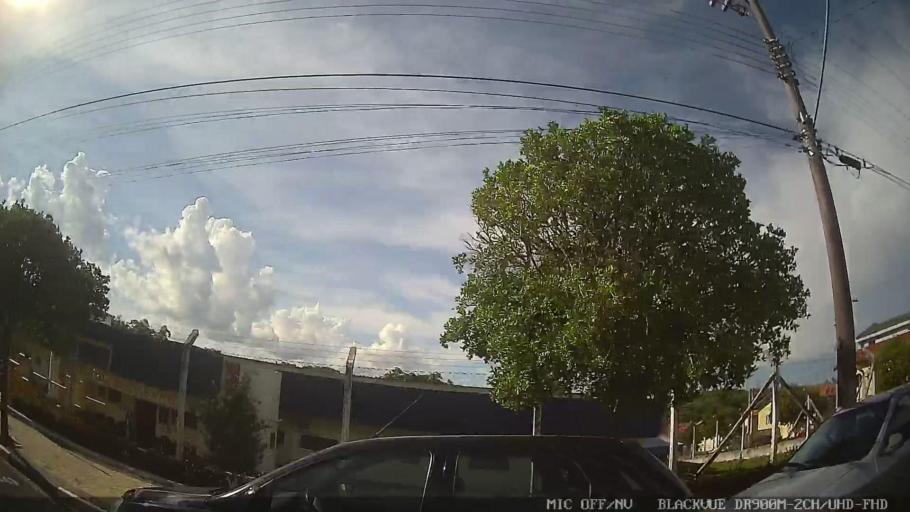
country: BR
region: Sao Paulo
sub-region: Laranjal Paulista
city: Laranjal Paulista
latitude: -23.0836
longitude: -47.7931
